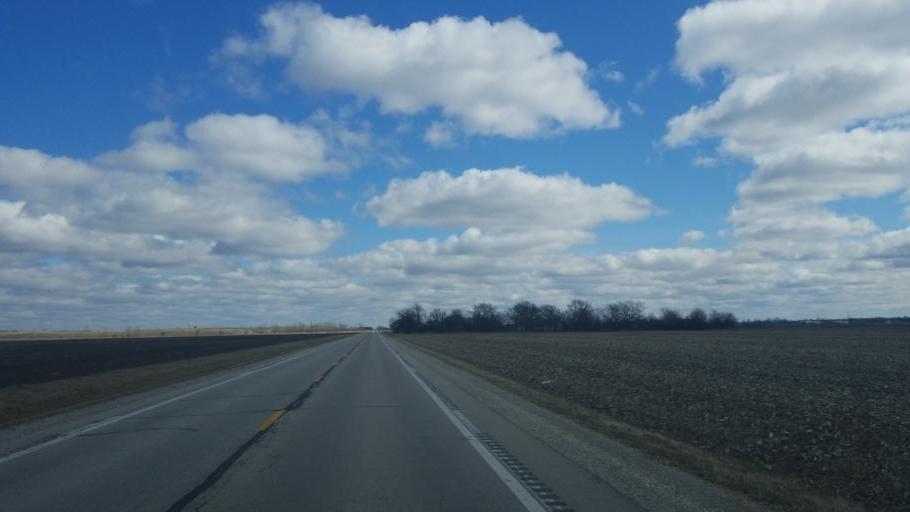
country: US
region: Illinois
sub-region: Douglas County
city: Villa Grove
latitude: 39.7921
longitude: -88.0714
